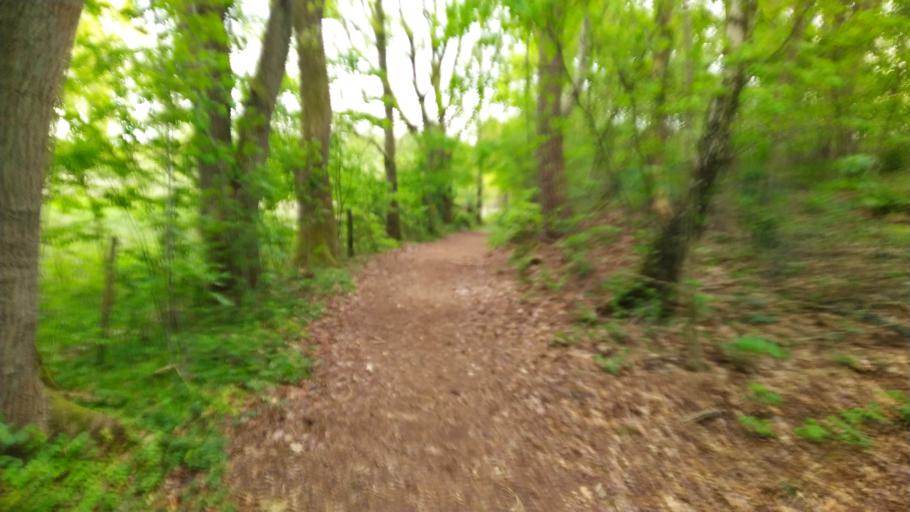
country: DE
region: Lower Saxony
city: Harsefeld
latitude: 53.4581
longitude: 9.4787
